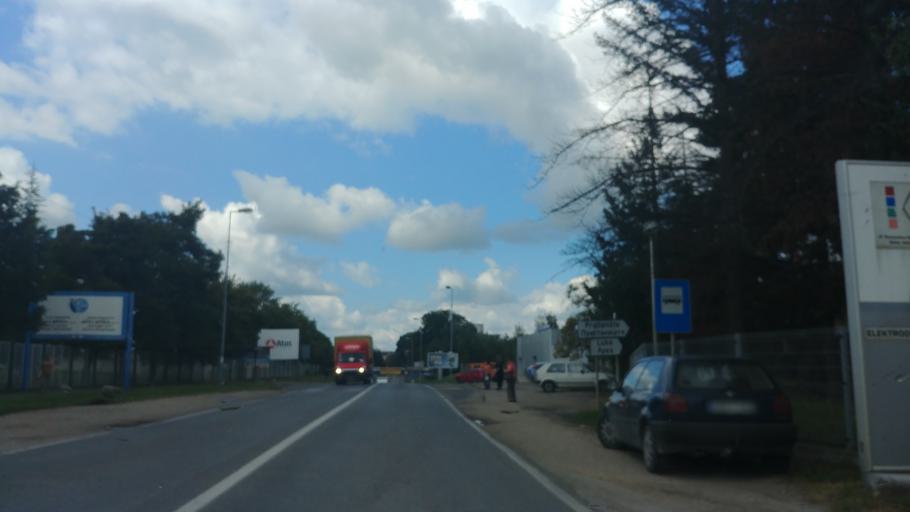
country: BA
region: Brcko
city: Brcko
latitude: 44.8634
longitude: 18.8217
